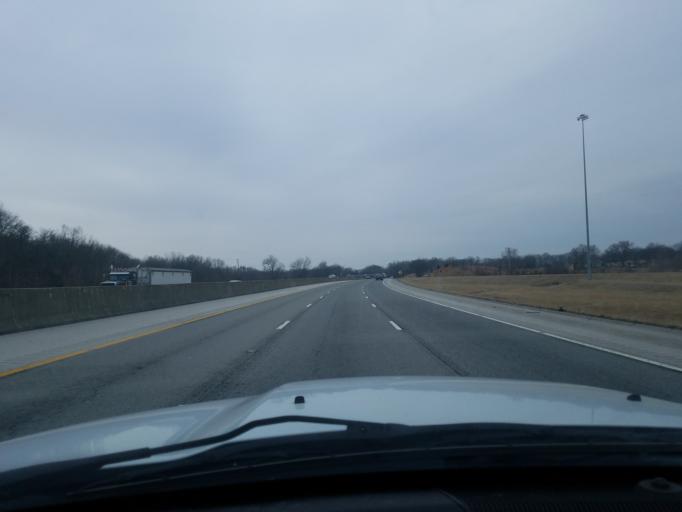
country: US
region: Kentucky
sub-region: Barren County
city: Cave City
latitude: 37.0566
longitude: -86.1179
